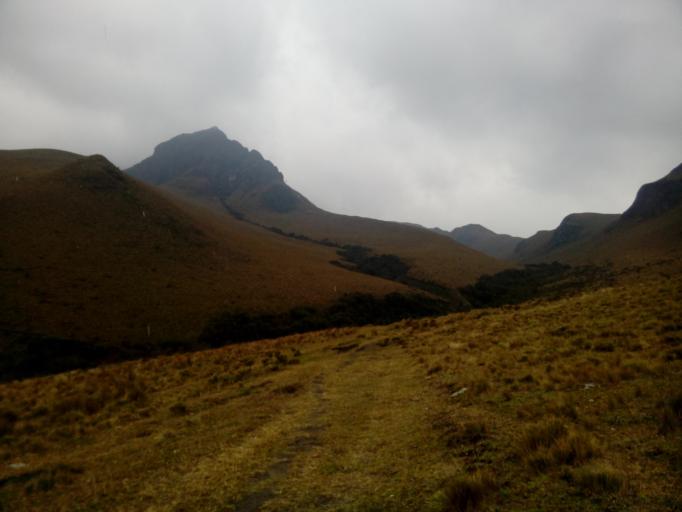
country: EC
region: Pichincha
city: Machachi
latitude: -0.5590
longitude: -78.5274
